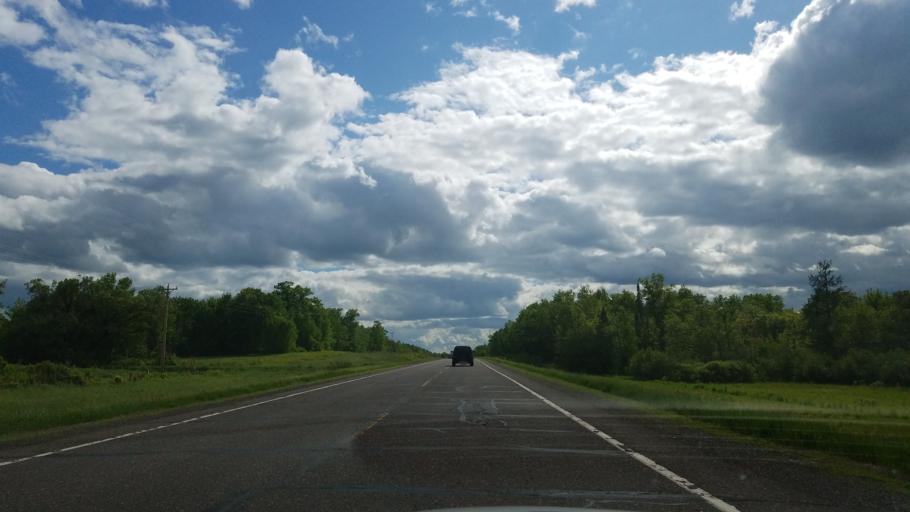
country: US
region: Wisconsin
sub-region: Burnett County
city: Siren
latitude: 46.1838
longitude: -92.1945
